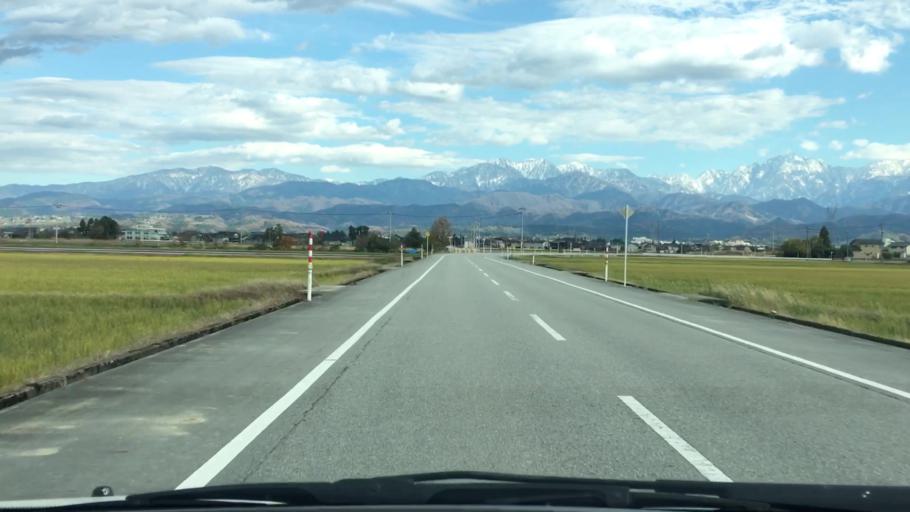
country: JP
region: Toyama
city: Kamiichi
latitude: 36.7087
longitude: 137.3205
